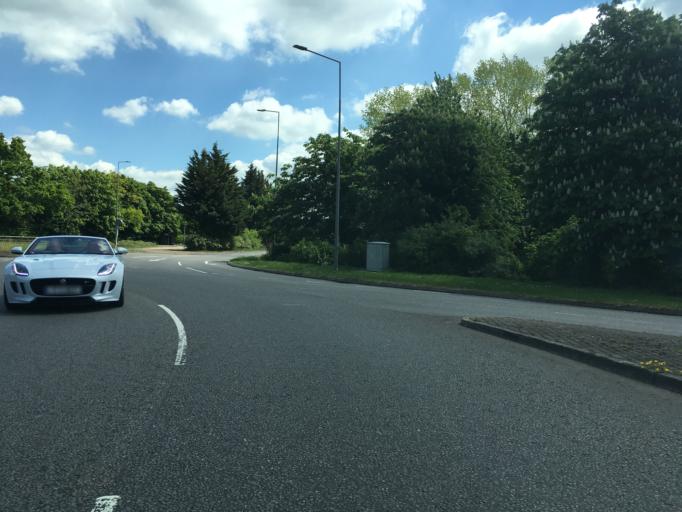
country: GB
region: England
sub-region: Milton Keynes
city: Milton Keynes
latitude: 52.0368
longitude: -0.7555
